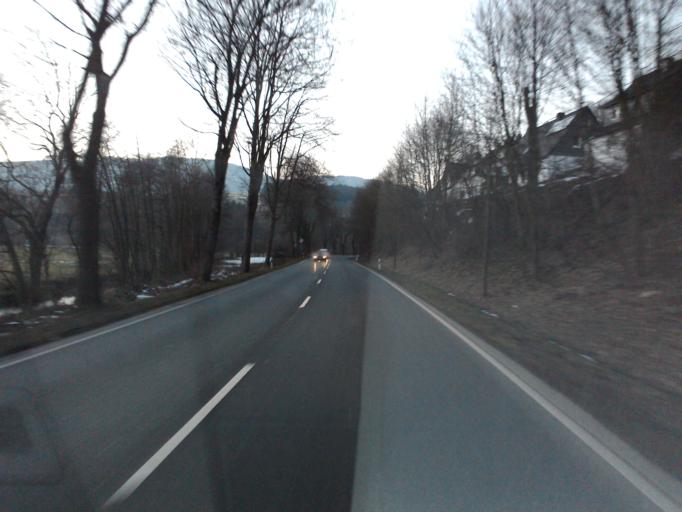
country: DE
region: North Rhine-Westphalia
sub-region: Regierungsbezirk Arnsberg
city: Olsberg
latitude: 51.3140
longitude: 8.5021
